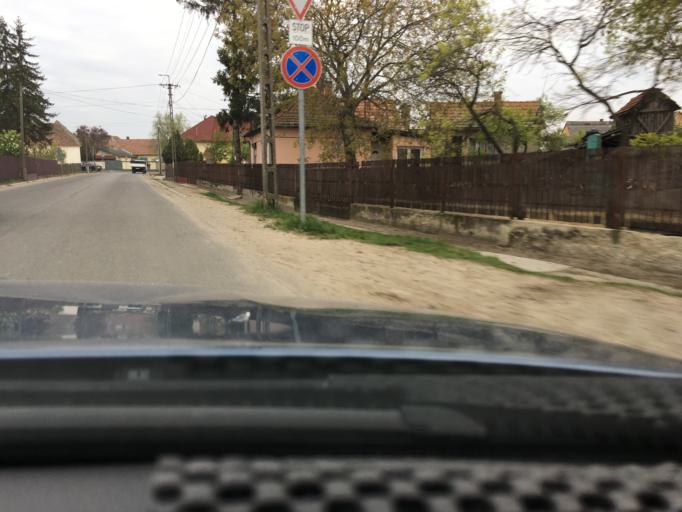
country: HU
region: Hajdu-Bihar
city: Hajdusamson
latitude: 47.5999
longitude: 21.7608
